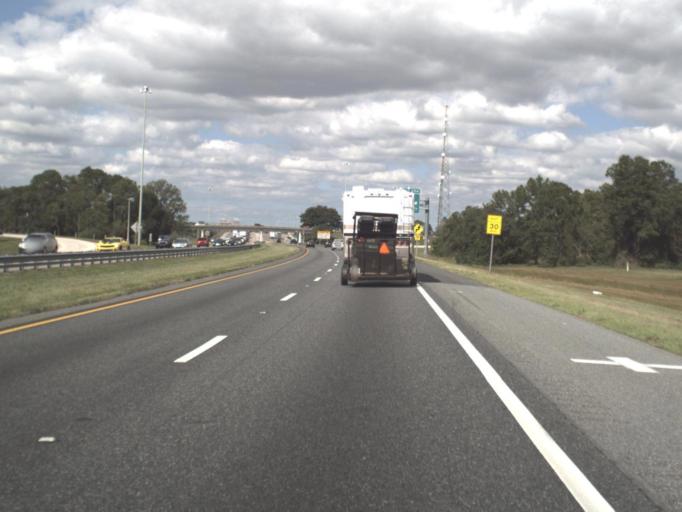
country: US
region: Florida
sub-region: Orange County
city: Taft
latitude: 28.4248
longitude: -81.3967
